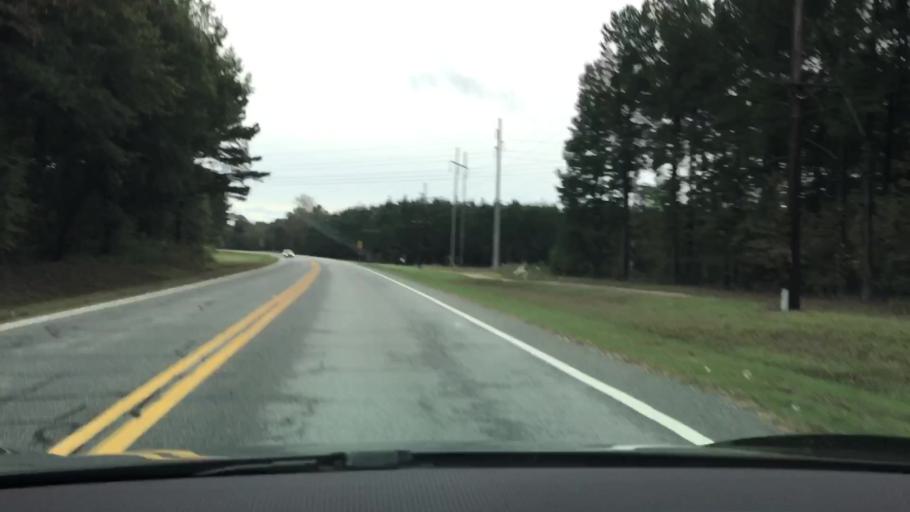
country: US
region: Georgia
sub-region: Warren County
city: Warrenton
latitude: 33.3915
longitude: -82.6471
